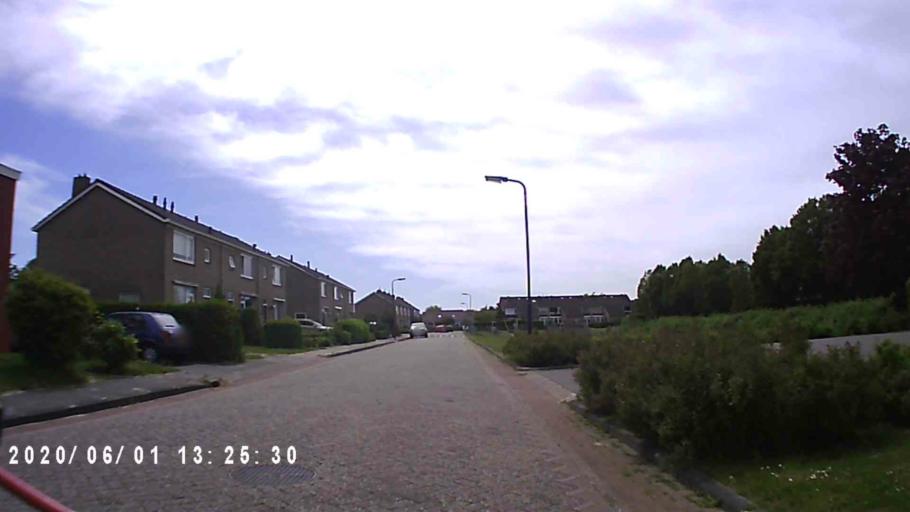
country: NL
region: Friesland
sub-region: Gemeente Littenseradiel
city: Wommels
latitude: 53.1074
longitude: 5.5821
